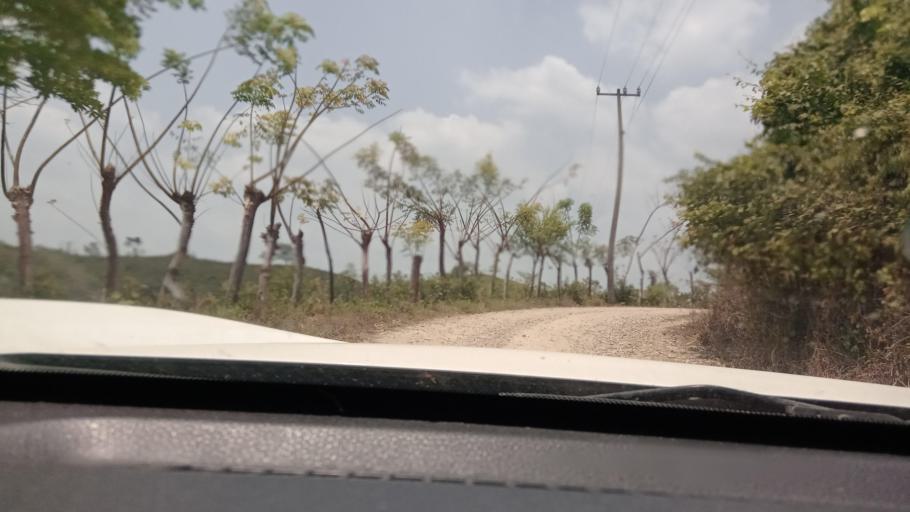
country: MX
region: Tabasco
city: Chontalpa
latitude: 17.5706
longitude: -93.7101
